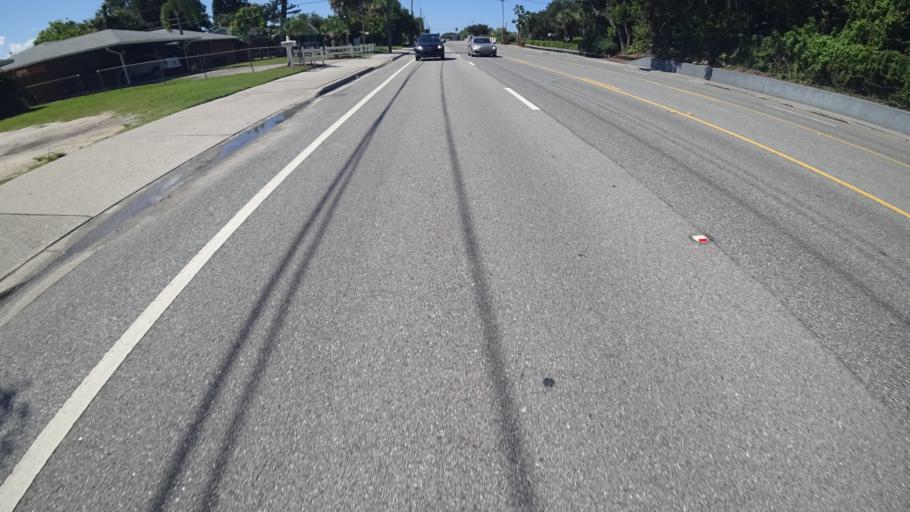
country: US
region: Florida
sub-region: Manatee County
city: South Bradenton
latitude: 27.4518
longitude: -82.5958
